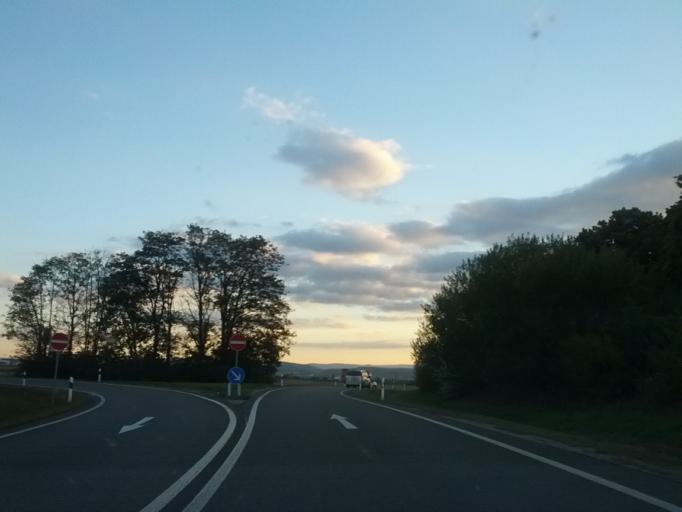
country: DE
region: Thuringia
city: Kirchheim
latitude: 50.9066
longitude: 11.0066
